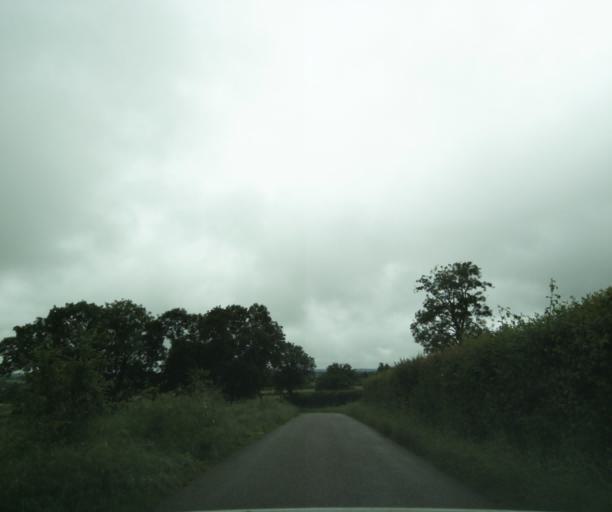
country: FR
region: Bourgogne
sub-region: Departement de Saone-et-Loire
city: Charolles
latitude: 46.4319
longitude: 4.3490
